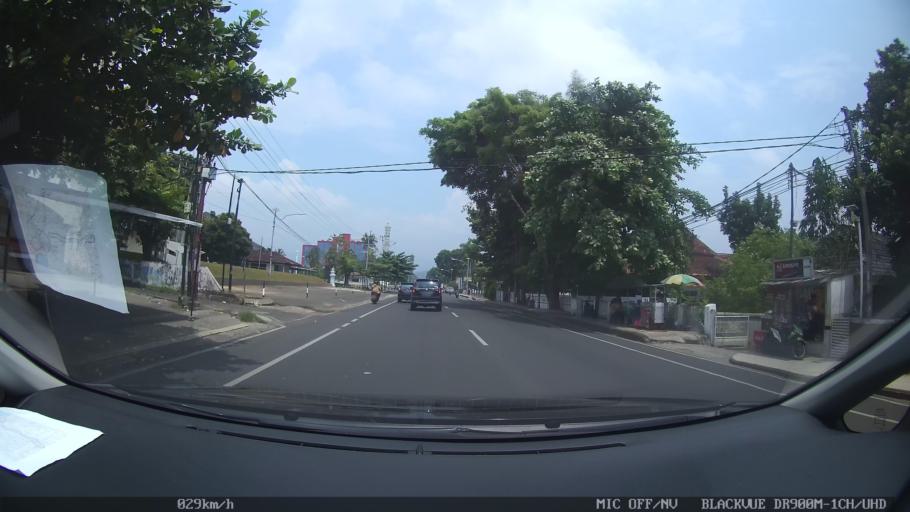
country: ID
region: Lampung
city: Bandarlampung
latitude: -5.4295
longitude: 105.2665
